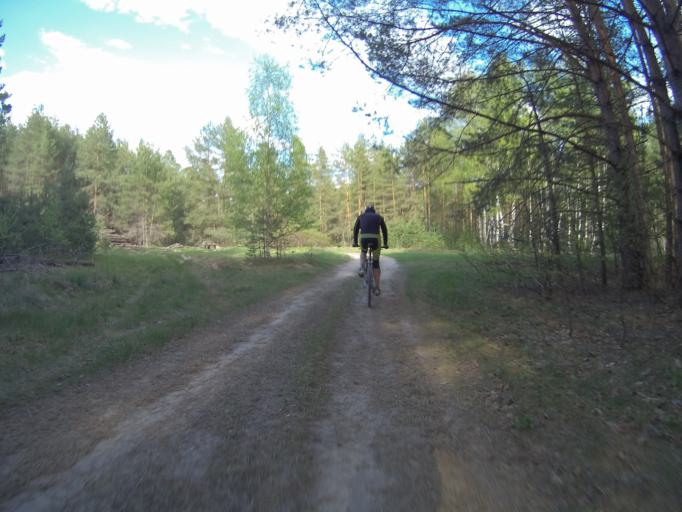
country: RU
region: Vladimir
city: Orgtrud
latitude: 56.1290
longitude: 40.7587
